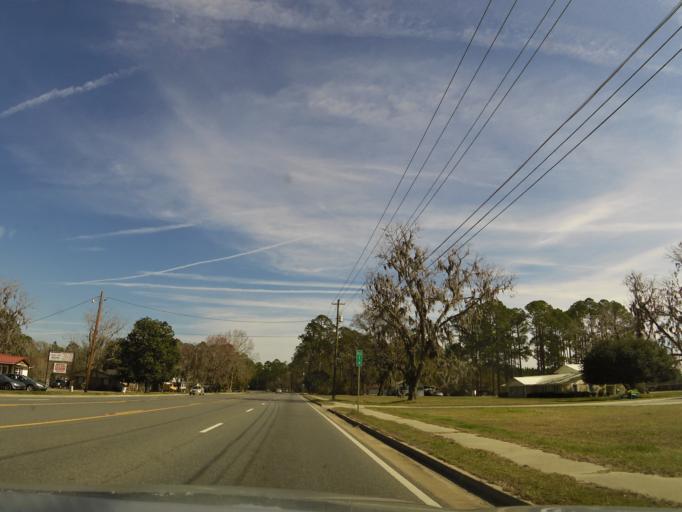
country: US
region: Georgia
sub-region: Brantley County
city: Nahunta
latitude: 31.2026
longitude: -81.9790
